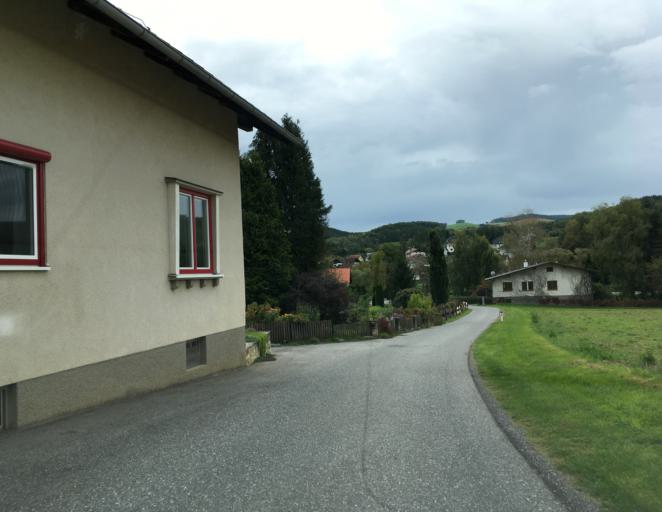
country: AT
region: Lower Austria
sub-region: Politischer Bezirk Wiener Neustadt
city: Bad Schonau
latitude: 47.4984
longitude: 16.2266
